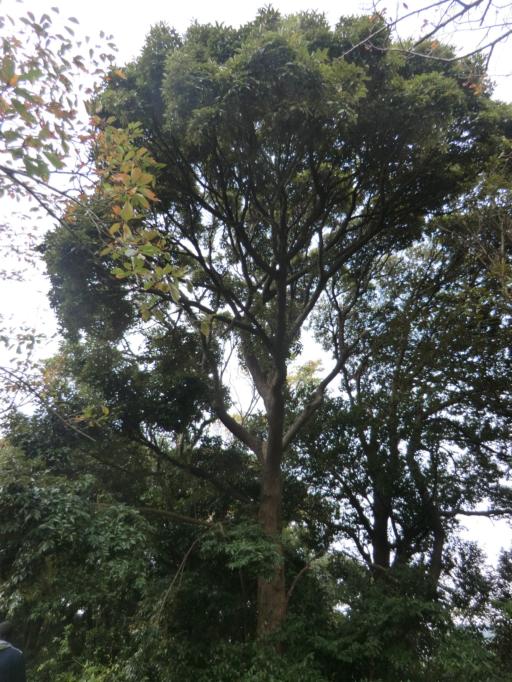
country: JP
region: Chiba
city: Futtsu
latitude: 35.1643
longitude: 139.8302
